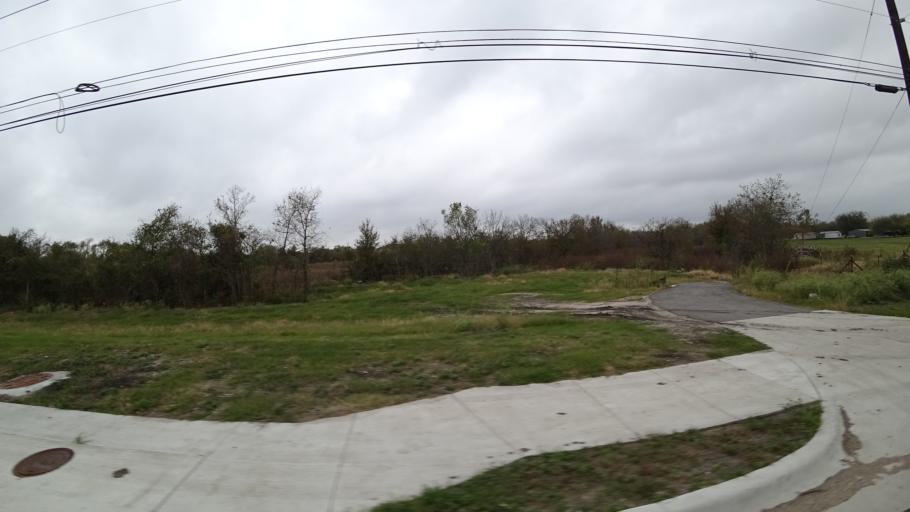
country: US
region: Texas
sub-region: Travis County
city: Windemere
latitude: 30.4720
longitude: -97.6210
